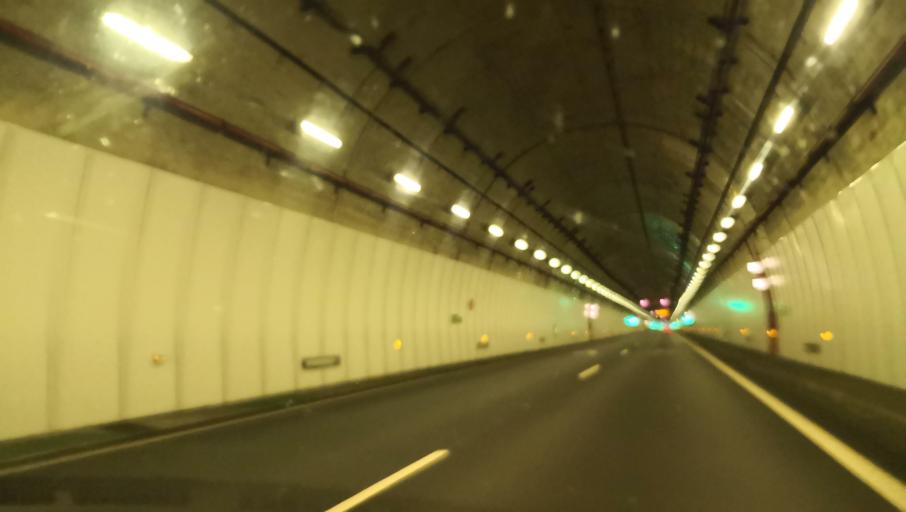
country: ES
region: Galicia
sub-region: Provincia de Pontevedra
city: Covelo
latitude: 42.1778
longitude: -8.3499
